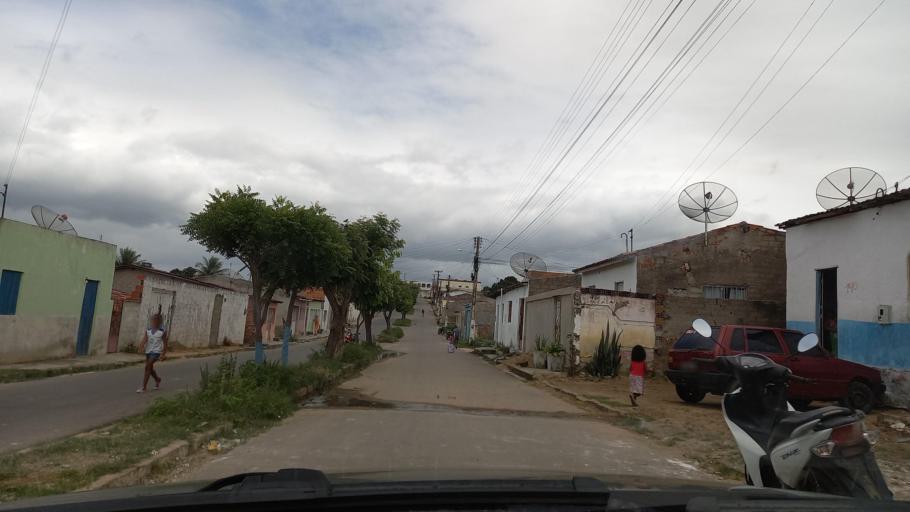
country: BR
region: Sergipe
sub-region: Caninde De Sao Francisco
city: Caninde de Sao Francisco
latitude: -9.6035
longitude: -37.7546
